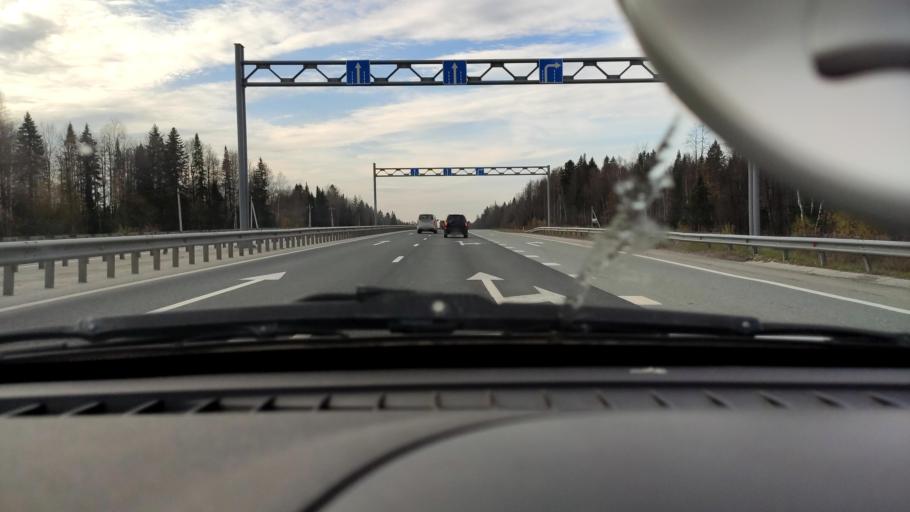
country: RU
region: Perm
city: Ferma
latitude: 58.0275
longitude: 56.4280
